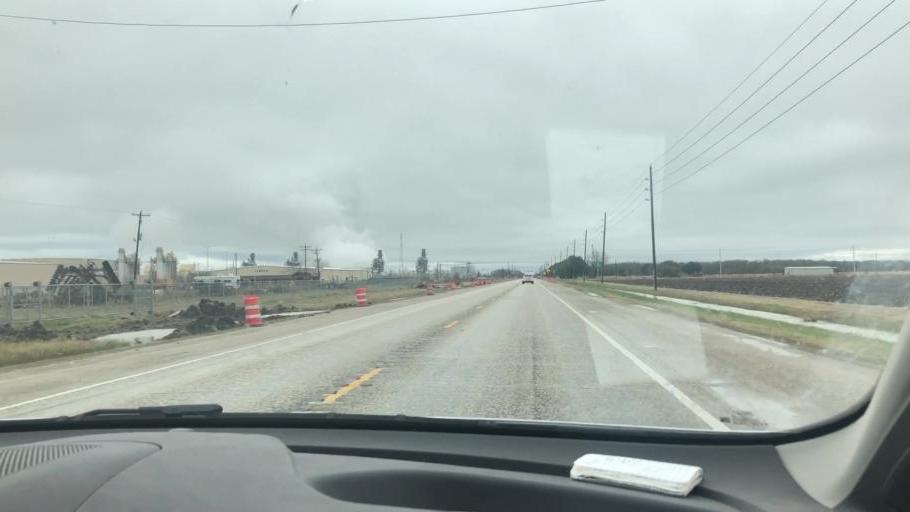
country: US
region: Texas
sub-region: Wharton County
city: Wharton
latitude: 29.2953
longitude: -96.0752
